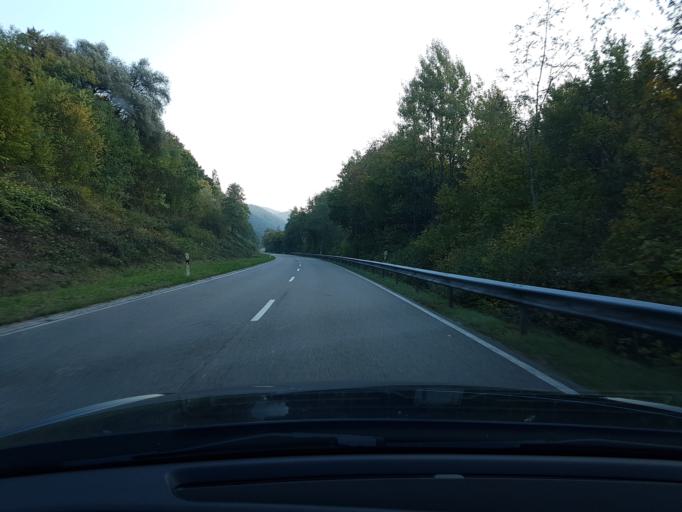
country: DE
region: Baden-Wuerttemberg
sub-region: Karlsruhe Region
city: Eberbach
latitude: 49.4916
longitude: 8.9640
